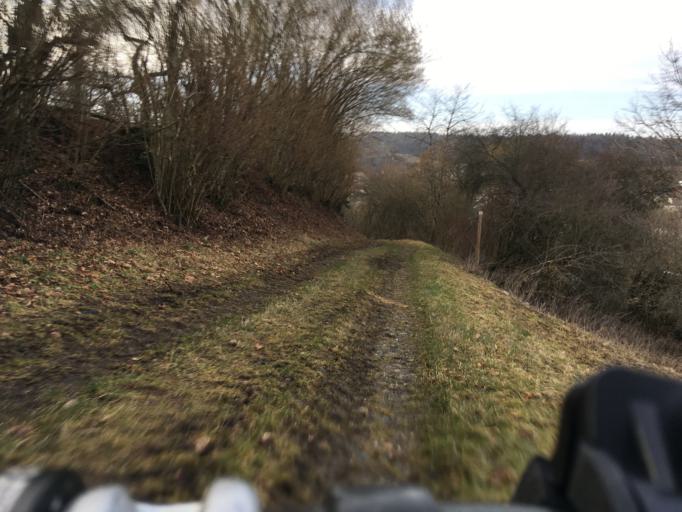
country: DE
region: Baden-Wuerttemberg
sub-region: Freiburg Region
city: Tengen
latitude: 47.7905
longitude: 8.6914
